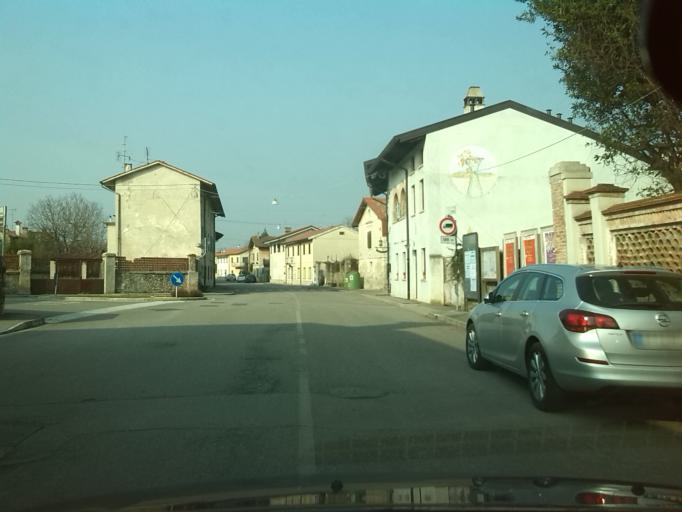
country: IT
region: Friuli Venezia Giulia
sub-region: Provincia di Gorizia
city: Moraro
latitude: 45.9215
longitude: 13.4820
